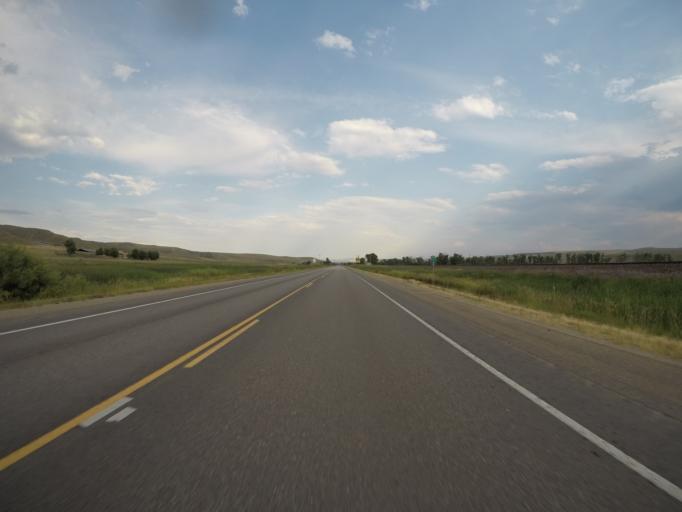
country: US
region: Colorado
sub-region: Moffat County
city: Craig
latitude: 40.5220
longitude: -107.4012
